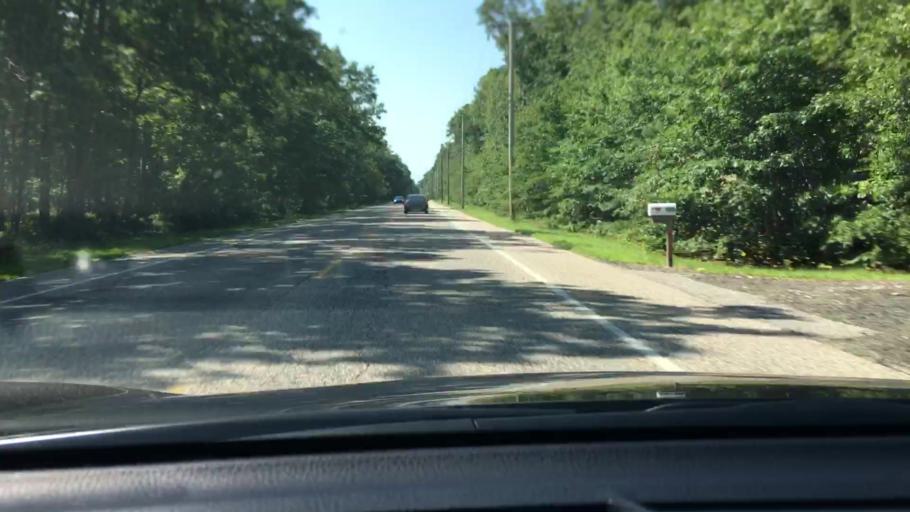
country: US
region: New Jersey
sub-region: Cape May County
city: Woodbine
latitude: 39.2654
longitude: -74.8024
